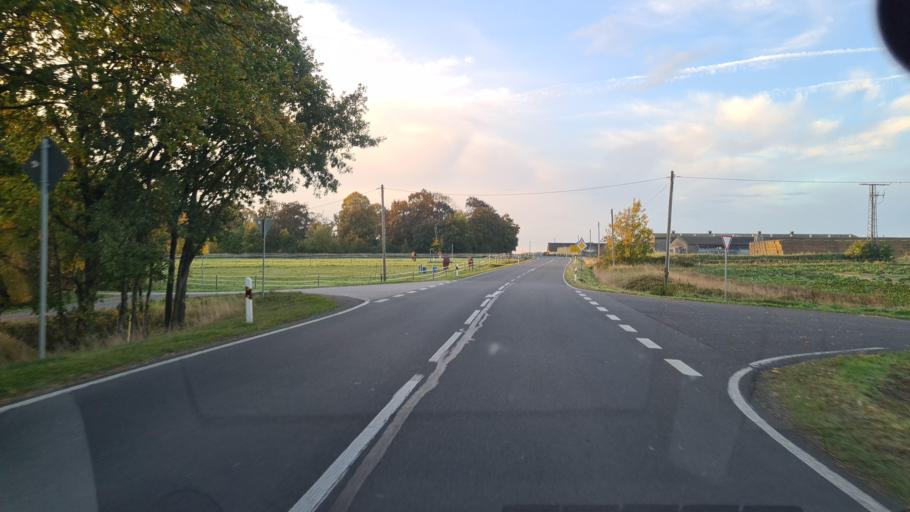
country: DE
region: Saxony
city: Machern
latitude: 51.4034
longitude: 12.6451
